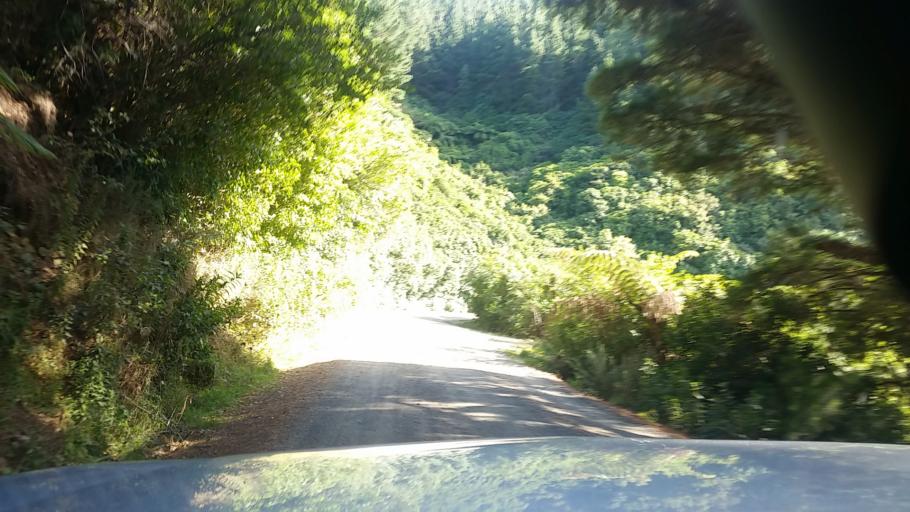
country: NZ
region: Marlborough
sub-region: Marlborough District
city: Picton
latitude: -41.2958
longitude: 174.1242
